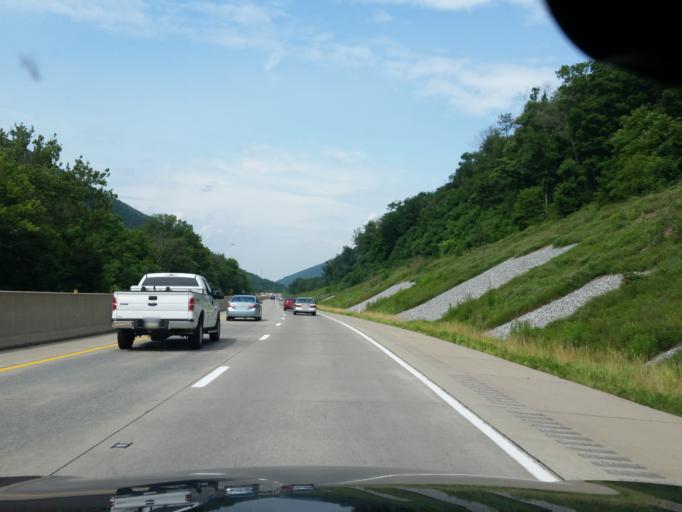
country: US
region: Pennsylvania
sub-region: Juniata County
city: Mifflintown
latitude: 40.6105
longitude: -77.4546
